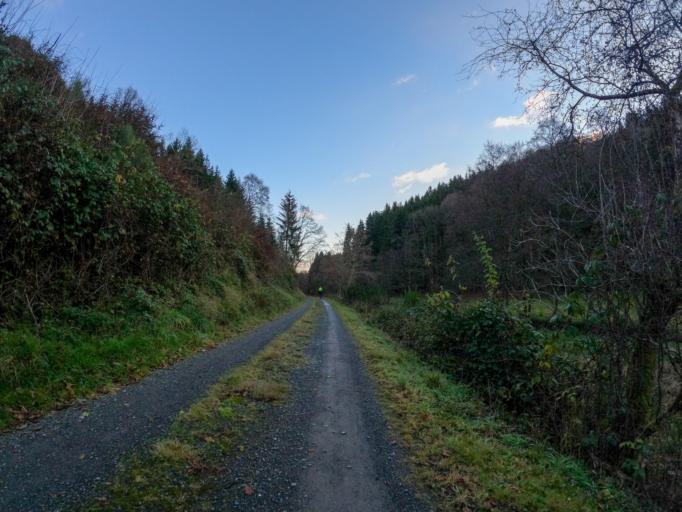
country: LU
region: Diekirch
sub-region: Canton de Wiltz
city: Bavigne
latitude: 49.9376
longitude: 5.8395
